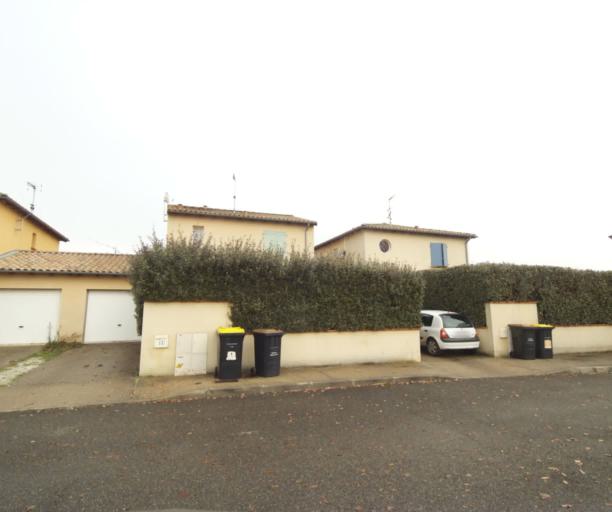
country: FR
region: Midi-Pyrenees
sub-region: Departement de la Haute-Garonne
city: Villemur-sur-Tarn
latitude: 43.8605
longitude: 1.4793
